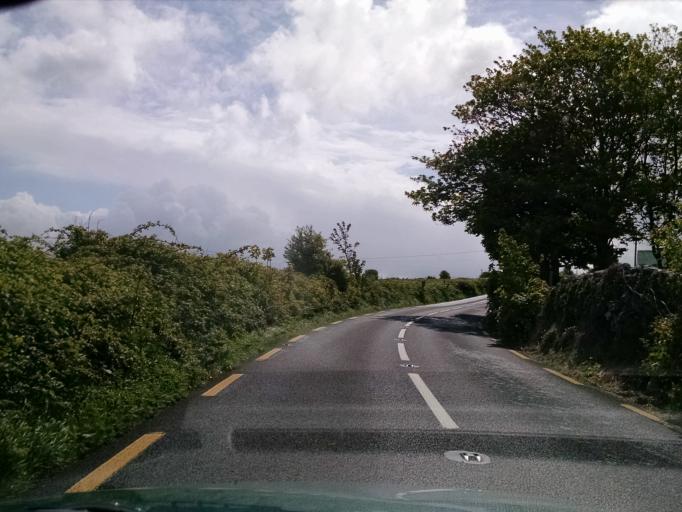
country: IE
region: Connaught
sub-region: County Galway
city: Gaillimh
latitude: 53.1424
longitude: -9.0270
